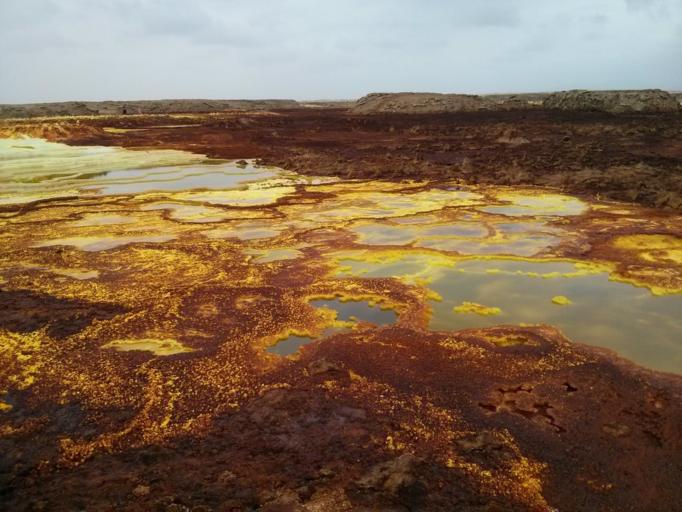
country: ET
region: Tigray
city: Adigrat
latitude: 14.2392
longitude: 40.2990
